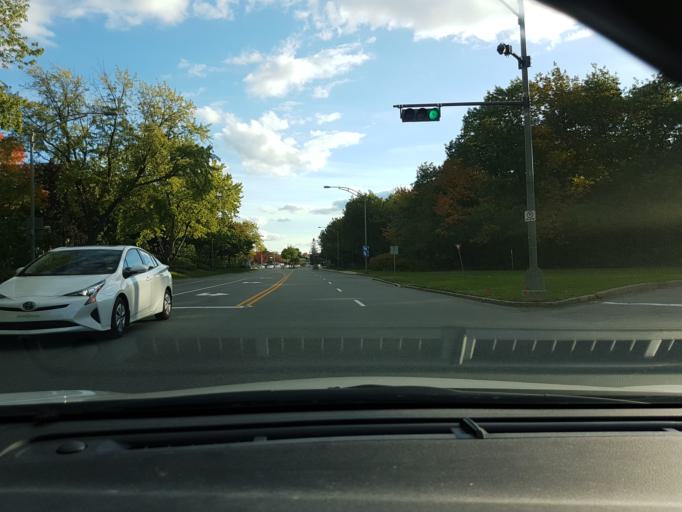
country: CA
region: Quebec
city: Quebec
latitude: 46.7820
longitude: -71.2645
